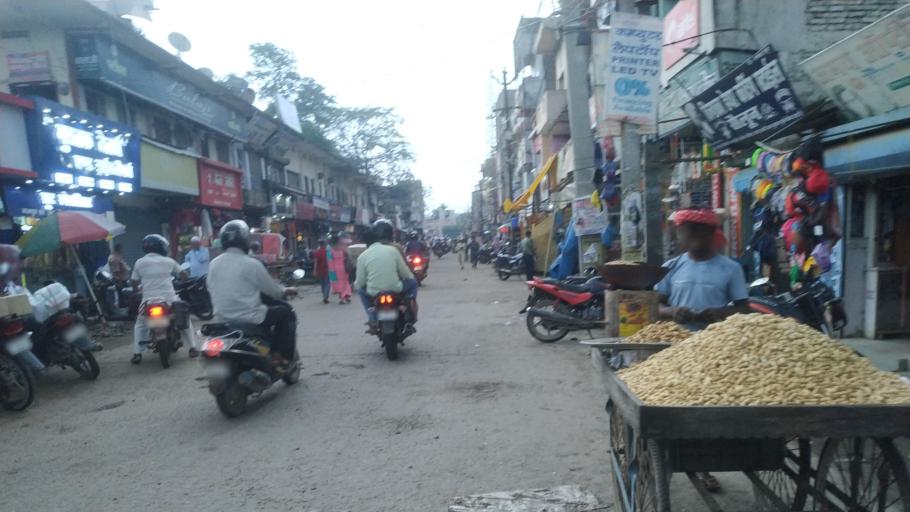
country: IN
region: Bihar
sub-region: Vaishali
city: Hajipur
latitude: 25.6924
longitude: 85.2119
